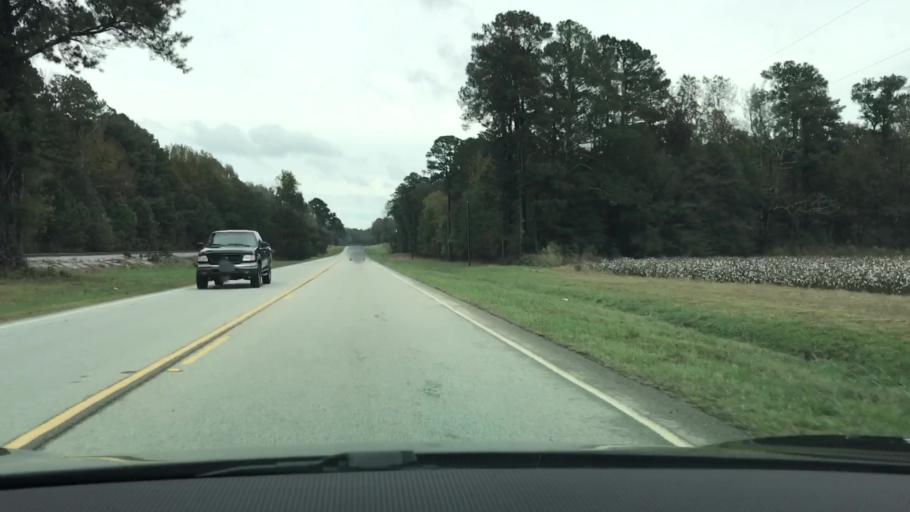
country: US
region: Georgia
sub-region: Warren County
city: Firing Range
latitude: 33.4732
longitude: -82.7252
